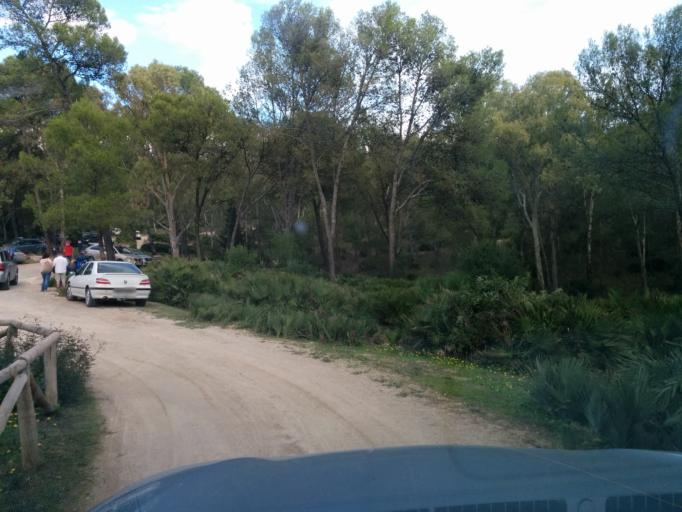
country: ES
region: Andalusia
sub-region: Provincia de Sevilla
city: Montellano
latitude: 37.0035
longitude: -5.5540
